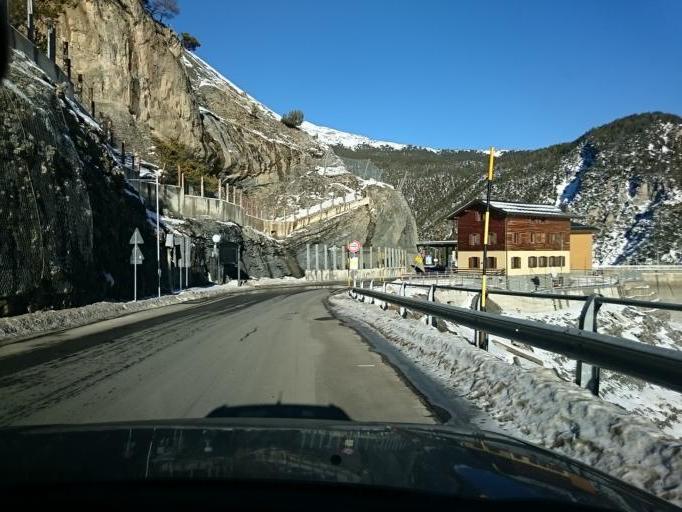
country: IT
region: Lombardy
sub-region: Provincia di Sondrio
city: Livigno
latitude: 46.6237
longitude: 10.1891
